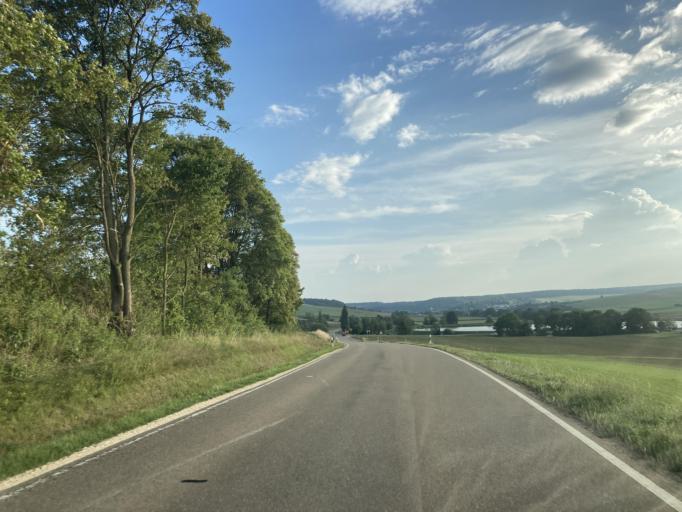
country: DE
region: Baden-Wuerttemberg
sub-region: Regierungsbezirk Stuttgart
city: Dischingen
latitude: 48.7192
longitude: 10.3836
